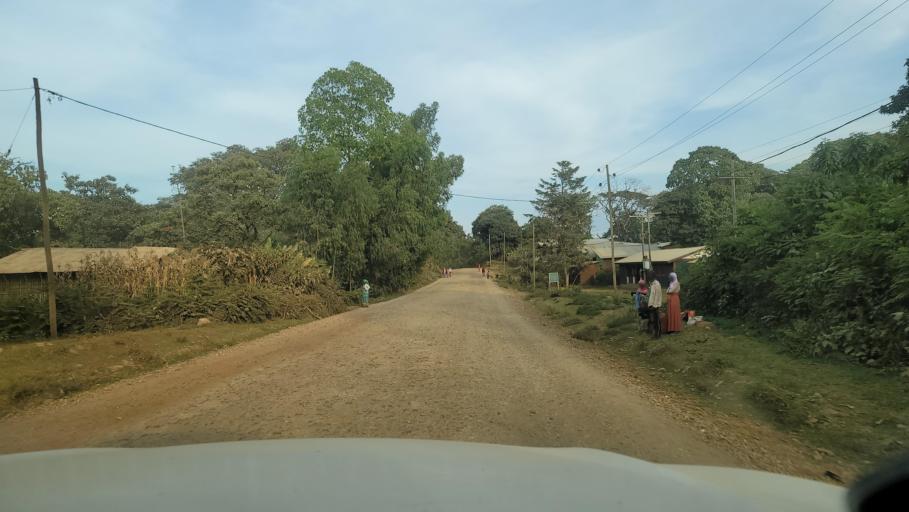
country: ET
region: Oromiya
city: Agaro
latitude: 7.8395
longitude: 36.5446
